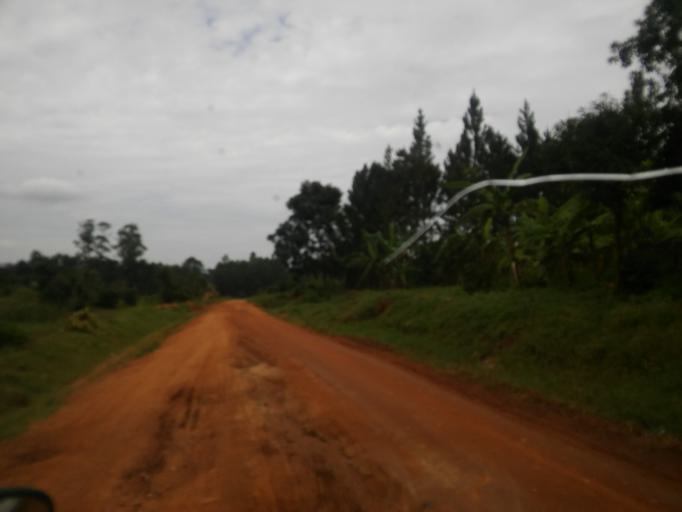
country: UG
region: Eastern Region
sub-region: Mbale District
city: Mbale
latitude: 0.9768
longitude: 34.2047
